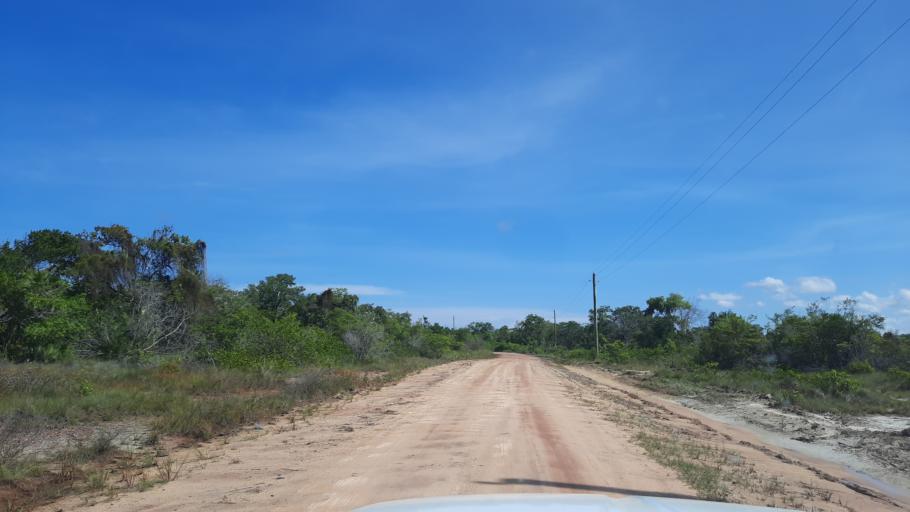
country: BZ
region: Stann Creek
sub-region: Dangriga
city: Dangriga
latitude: 17.1677
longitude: -88.3298
